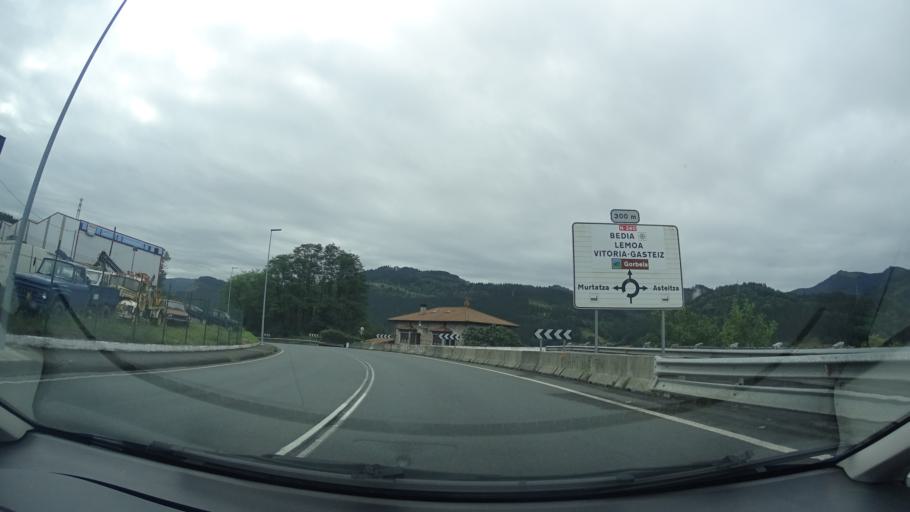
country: ES
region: Basque Country
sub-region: Bizkaia
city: Galdakao
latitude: 43.2116
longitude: -2.8099
